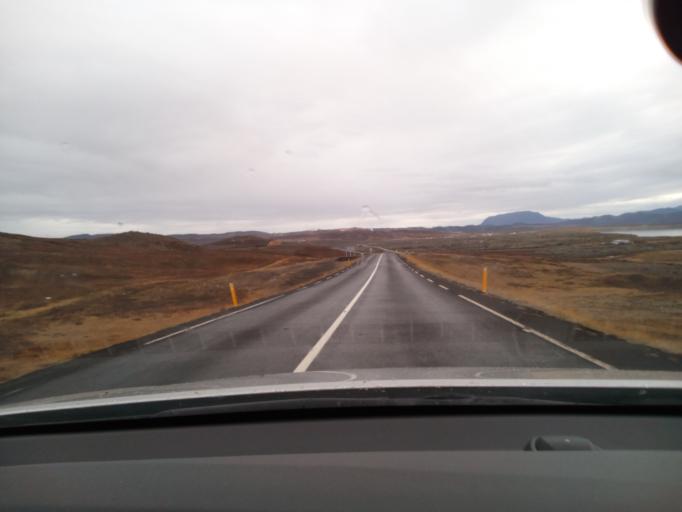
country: IS
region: Northeast
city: Laugar
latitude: 65.6604
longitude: -16.9739
